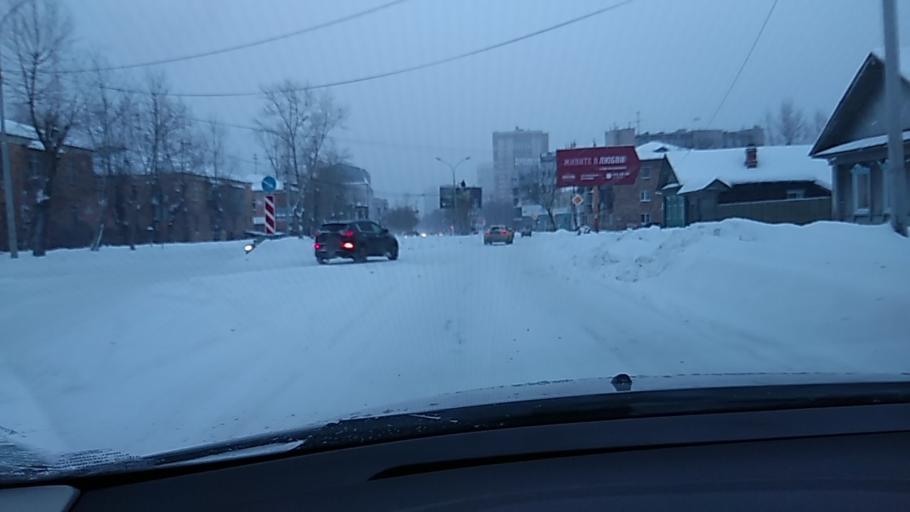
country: RU
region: Sverdlovsk
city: Sovkhoznyy
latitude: 56.8212
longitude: 60.5526
